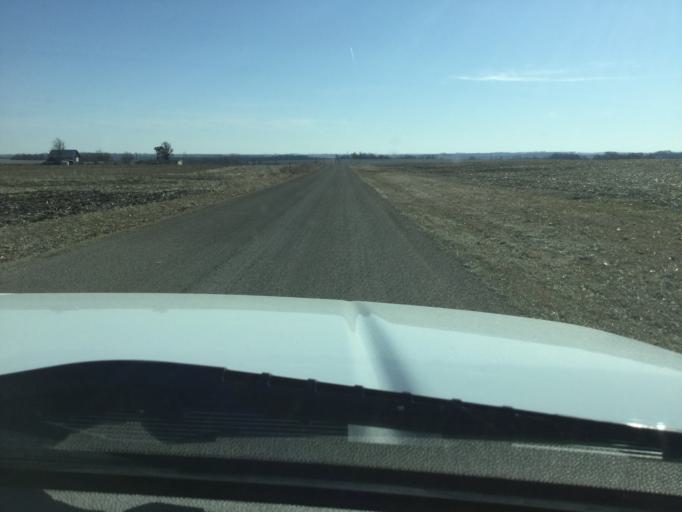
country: US
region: Kansas
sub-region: Brown County
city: Horton
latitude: 39.7256
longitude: -95.4389
